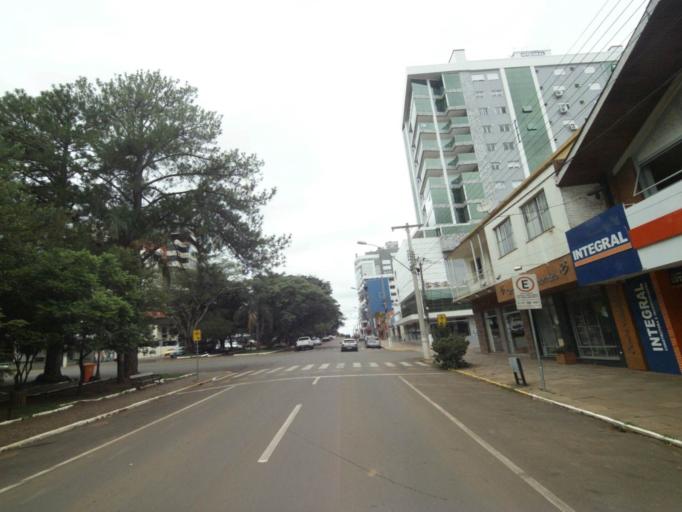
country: BR
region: Rio Grande do Sul
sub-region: Lagoa Vermelha
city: Lagoa Vermelha
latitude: -28.2107
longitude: -51.5223
